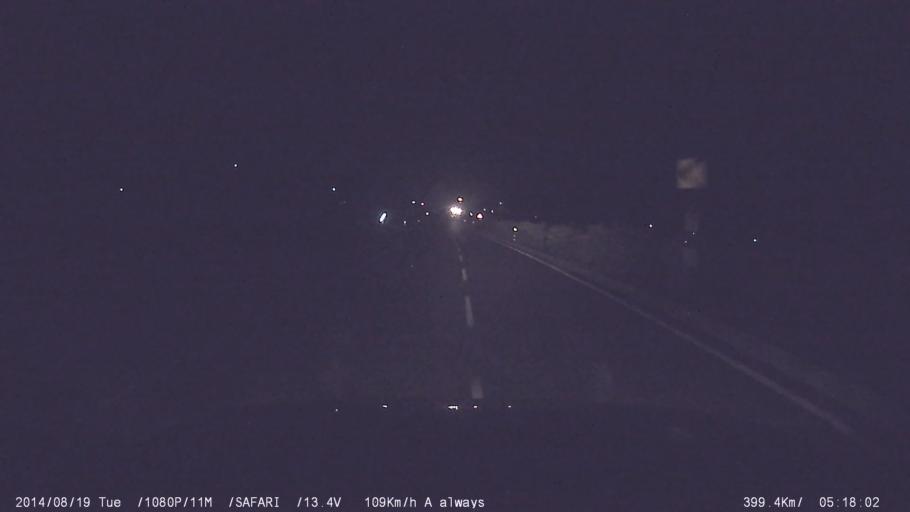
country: IN
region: Tamil Nadu
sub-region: Salem
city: Konganapuram
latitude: 11.5218
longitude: 77.9400
